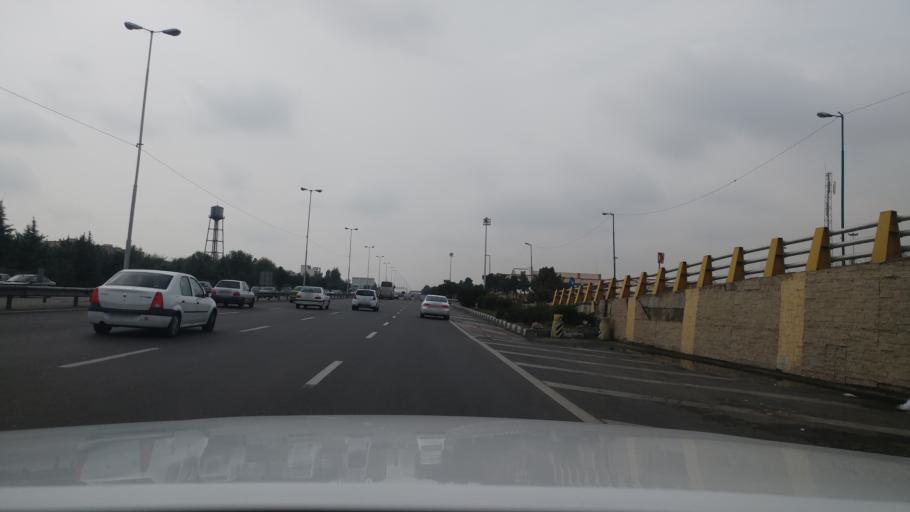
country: IR
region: Tehran
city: Tehran
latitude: 35.7161
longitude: 51.2846
